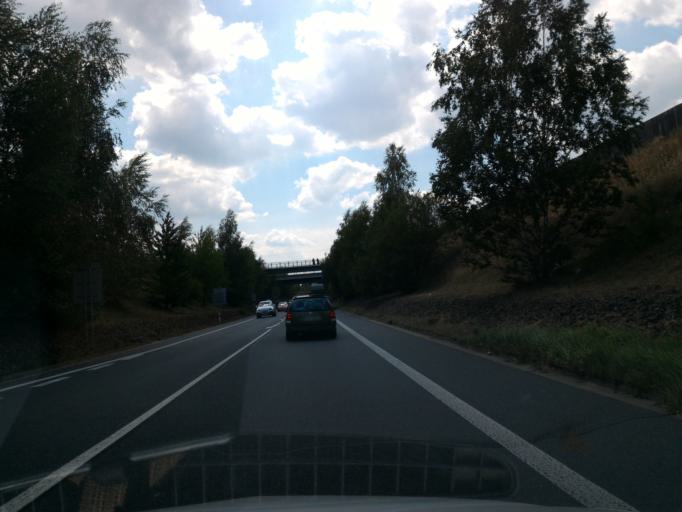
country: CZ
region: Central Bohemia
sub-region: Okres Kutna Hora
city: Caslav
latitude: 49.9050
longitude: 15.4062
